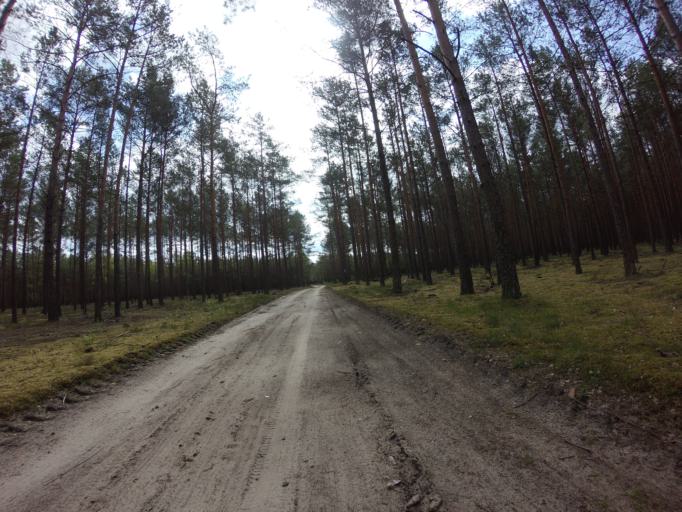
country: PL
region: West Pomeranian Voivodeship
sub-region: Powiat drawski
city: Kalisz Pomorski
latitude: 53.2029
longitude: 15.9880
